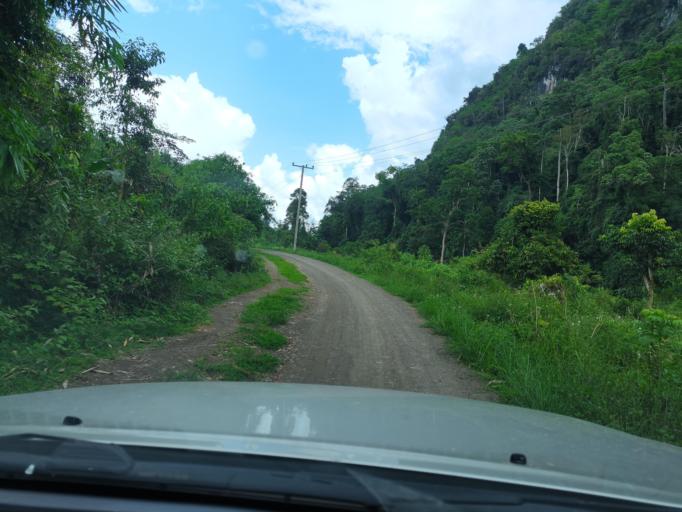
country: LA
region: Loungnamtha
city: Muang Long
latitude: 20.7802
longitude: 101.0162
